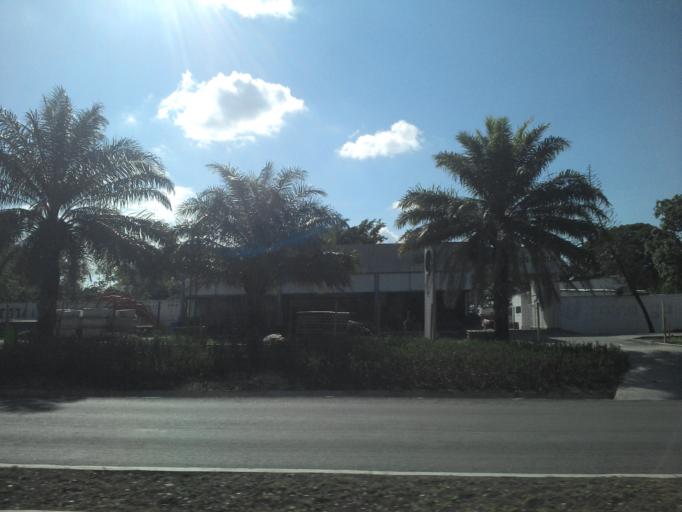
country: MX
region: Chiapas
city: Palenque
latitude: 17.5275
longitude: -91.9922
